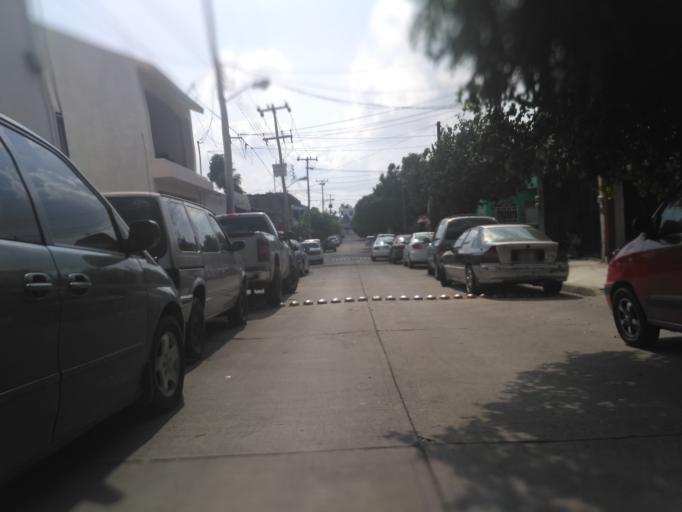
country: MX
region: Sinaloa
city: Culiacan
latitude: 24.7949
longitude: -107.4015
